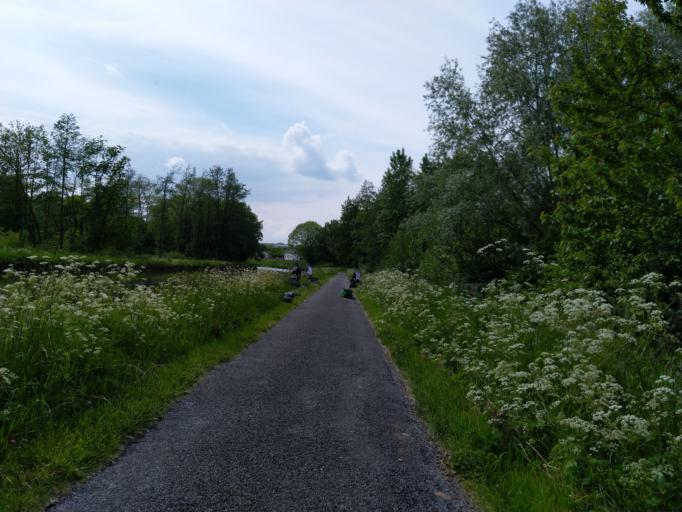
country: FR
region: Picardie
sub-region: Departement de l'Aisne
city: Etreux
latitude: 49.9966
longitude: 3.6710
